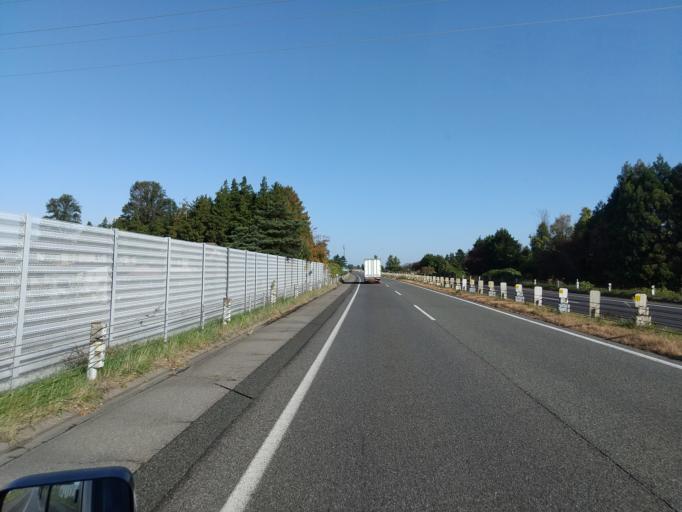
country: JP
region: Iwate
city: Hanamaki
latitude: 39.3353
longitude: 141.0912
